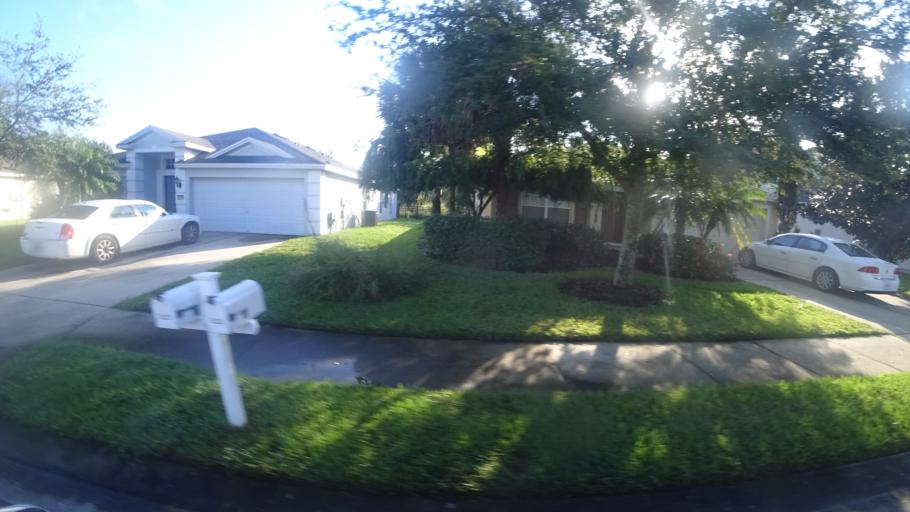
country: US
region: Florida
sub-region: Manatee County
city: Ellenton
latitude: 27.5611
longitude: -82.4599
